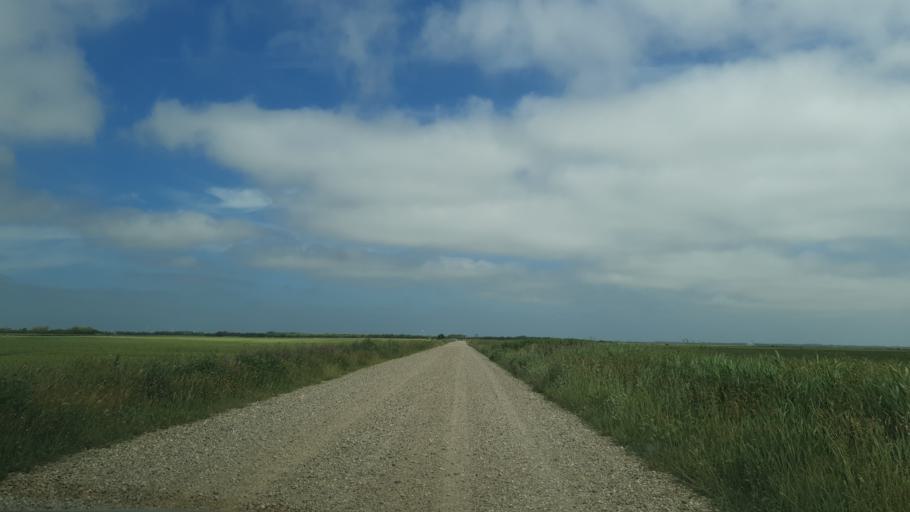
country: DK
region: Central Jutland
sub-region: Ringkobing-Skjern Kommune
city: Skjern
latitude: 55.9351
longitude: 8.4290
